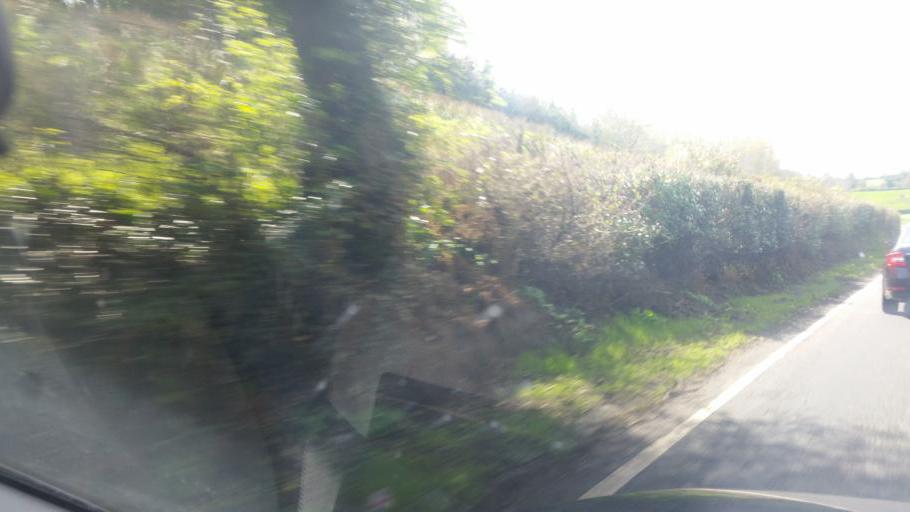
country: GB
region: Northern Ireland
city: Irvinestown
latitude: 54.4501
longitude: -7.8011
